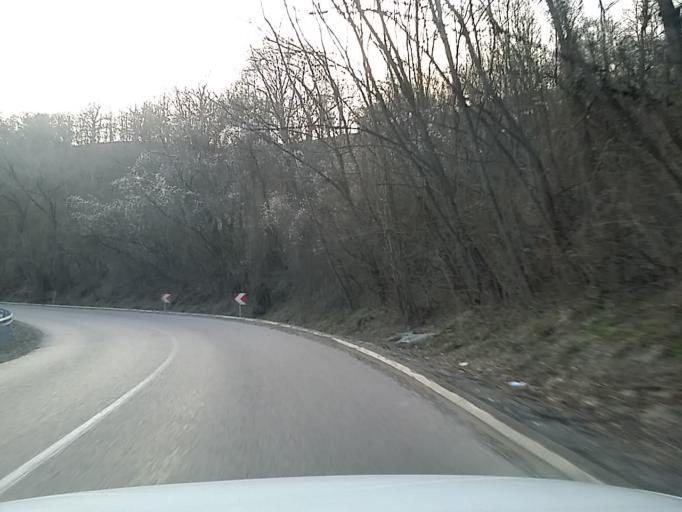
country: HU
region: Borsod-Abauj-Zemplen
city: Borsodnadasd
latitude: 48.1036
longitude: 20.2291
